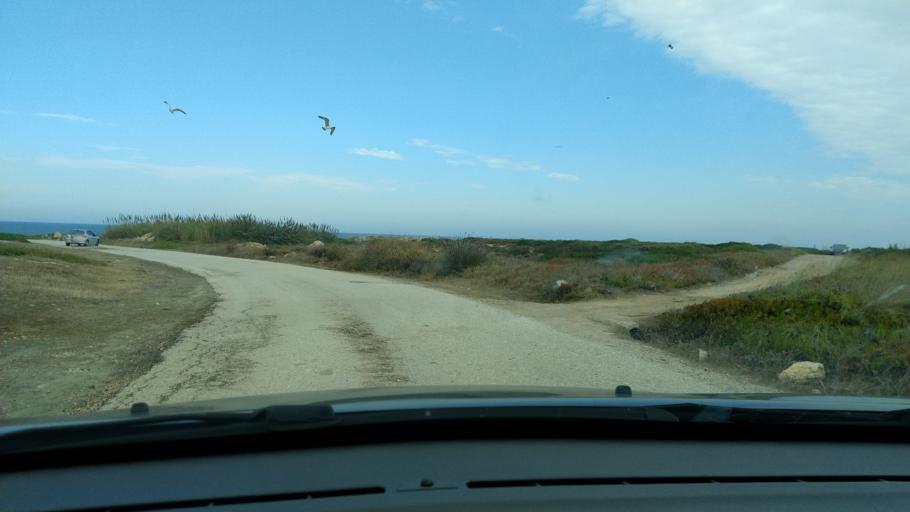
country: PT
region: Leiria
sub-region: Peniche
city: Peniche
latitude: 39.3661
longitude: -9.4008
